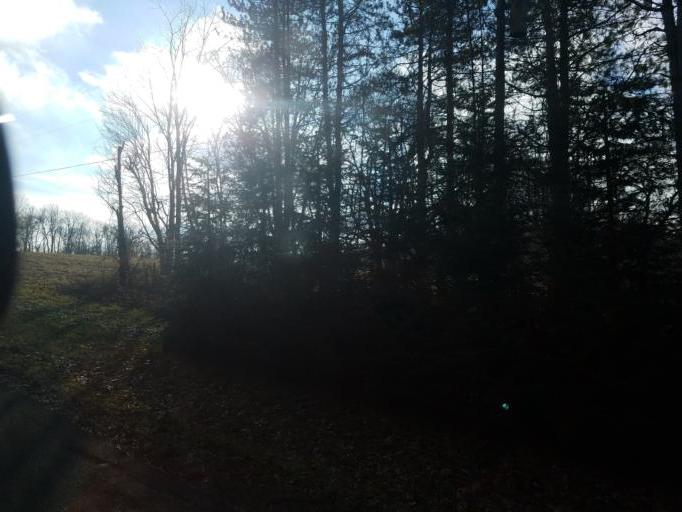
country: US
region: Ohio
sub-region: Sandusky County
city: Bellville
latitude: 40.5741
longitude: -82.3761
